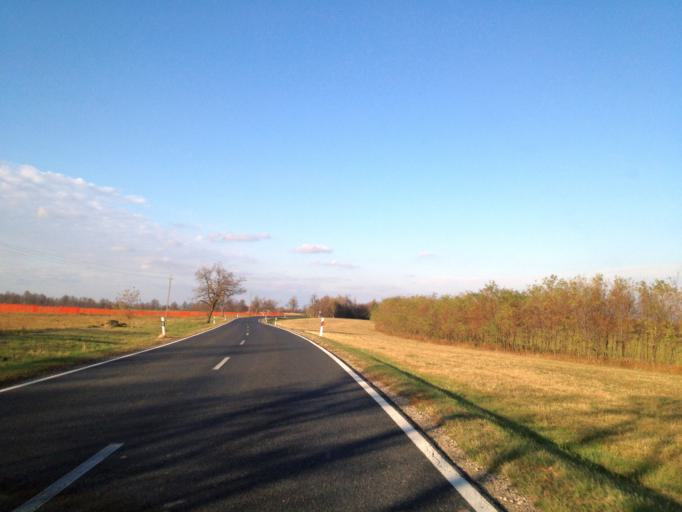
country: HU
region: Veszprem
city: Zirc
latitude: 47.3215
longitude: 17.8761
